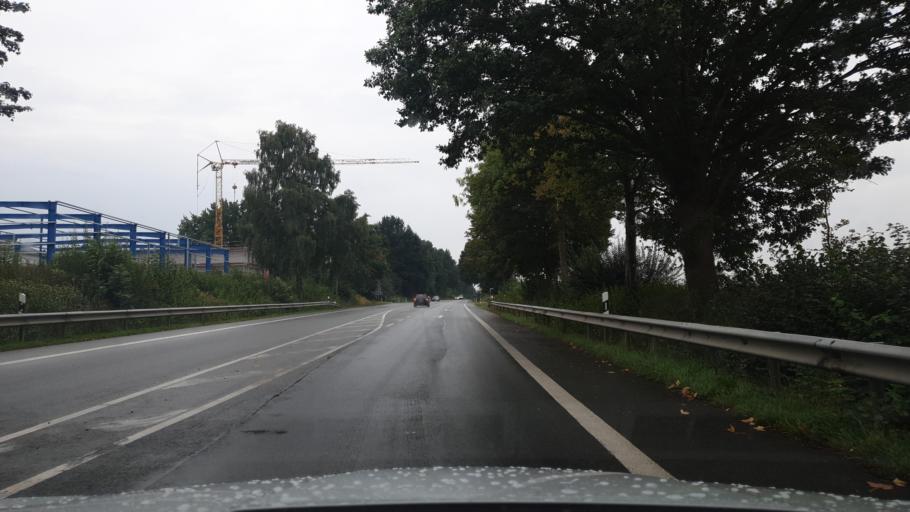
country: DE
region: North Rhine-Westphalia
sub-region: Regierungsbezirk Detmold
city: Kirchlengern
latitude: 52.2386
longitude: 8.6380
